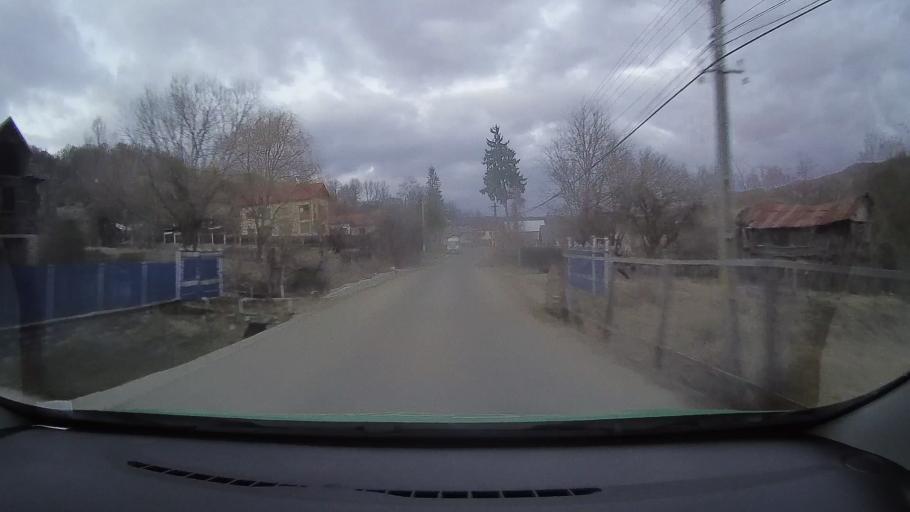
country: RO
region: Dambovita
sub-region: Comuna Visinesti
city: Visinesti
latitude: 45.1014
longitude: 25.5803
